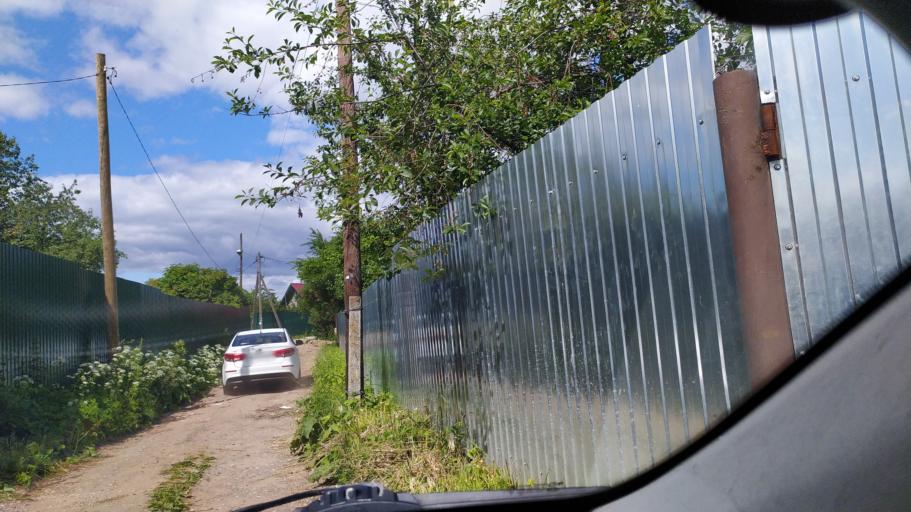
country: RU
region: Chuvashia
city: Novyye Lapsary
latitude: 56.1132
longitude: 47.1742
